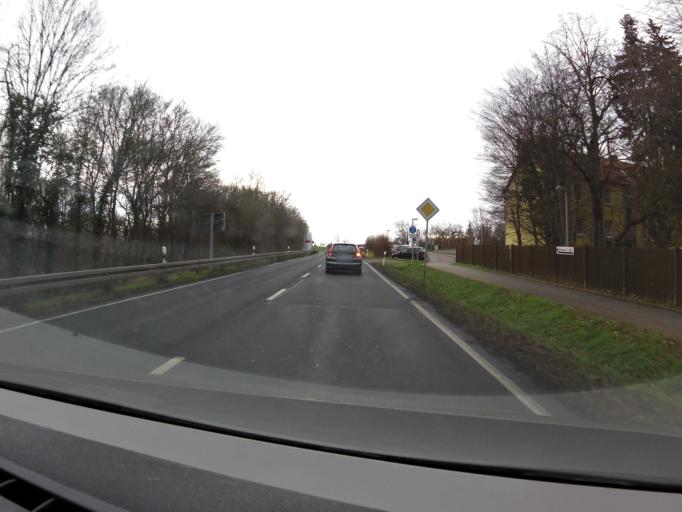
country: DE
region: Saxony-Anhalt
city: Aschersleben
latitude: 51.7452
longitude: 11.4581
